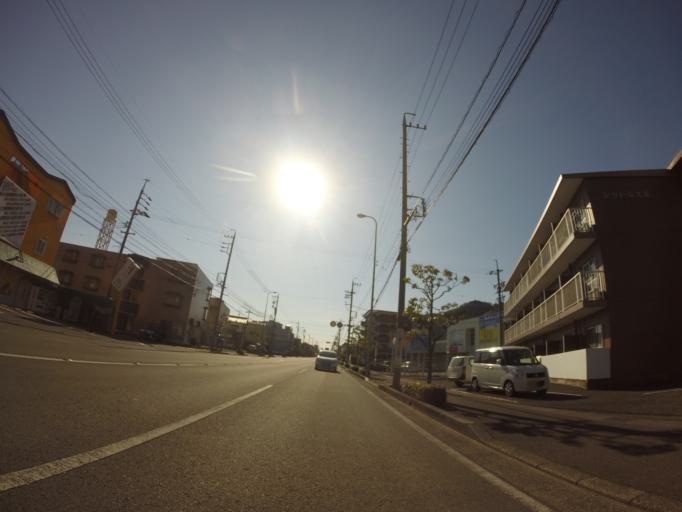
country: JP
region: Shizuoka
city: Shizuoka-shi
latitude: 35.0009
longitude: 138.3804
